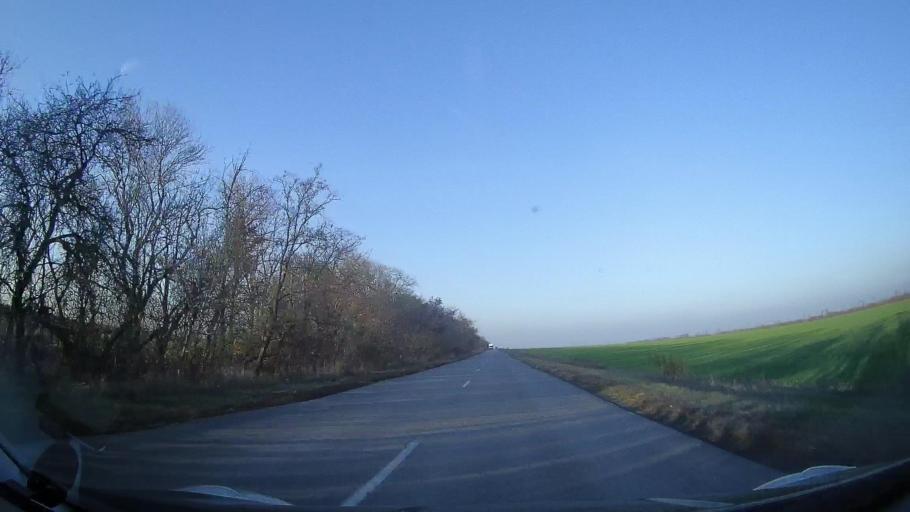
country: RU
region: Rostov
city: Kirovskaya
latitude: 47.0060
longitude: 39.9790
